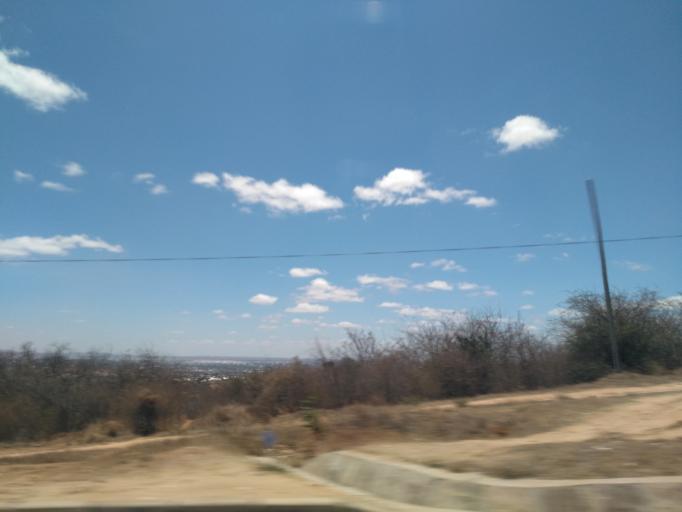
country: TZ
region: Dodoma
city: Kisasa
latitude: -6.2146
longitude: 35.7932
